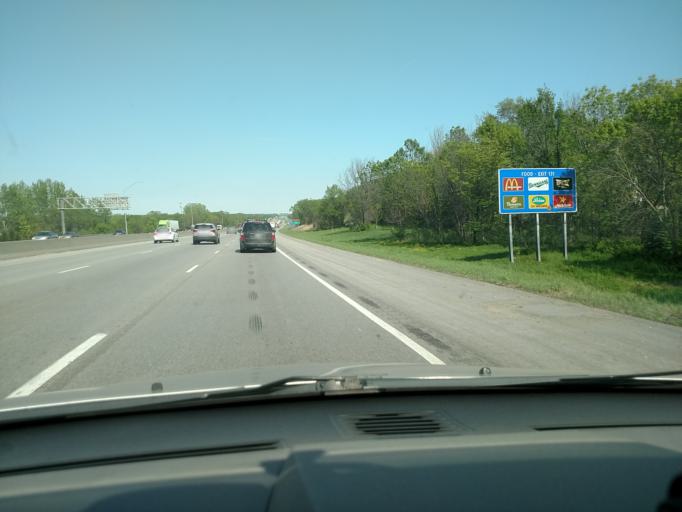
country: US
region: Iowa
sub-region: Polk County
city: Urbandale
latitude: 41.6527
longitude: -93.7149
